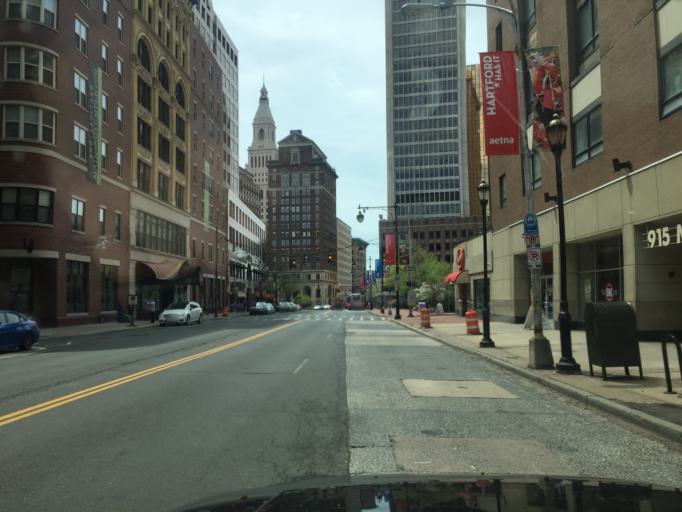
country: US
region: Connecticut
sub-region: Hartford County
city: Hartford
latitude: 41.7680
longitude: -72.6732
